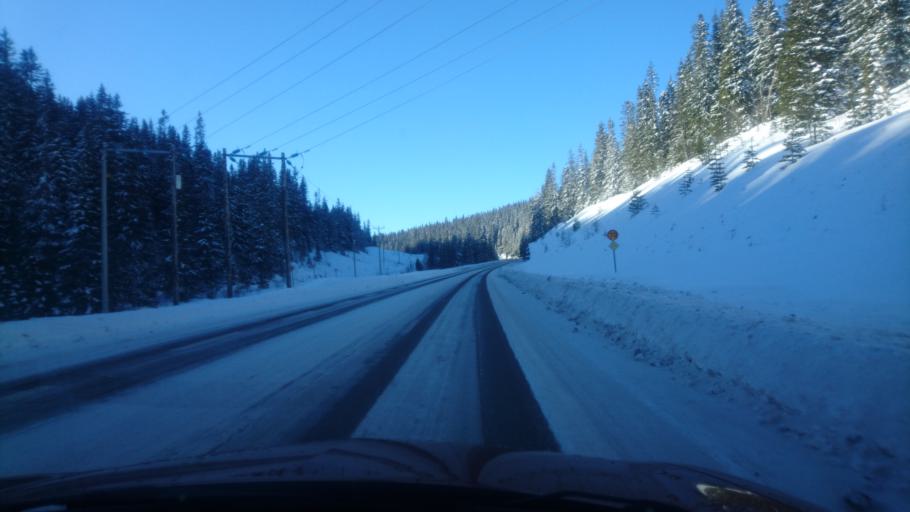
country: SE
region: Dalarna
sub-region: Malung-Saelens kommun
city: Malung
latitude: 61.1679
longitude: 13.1574
